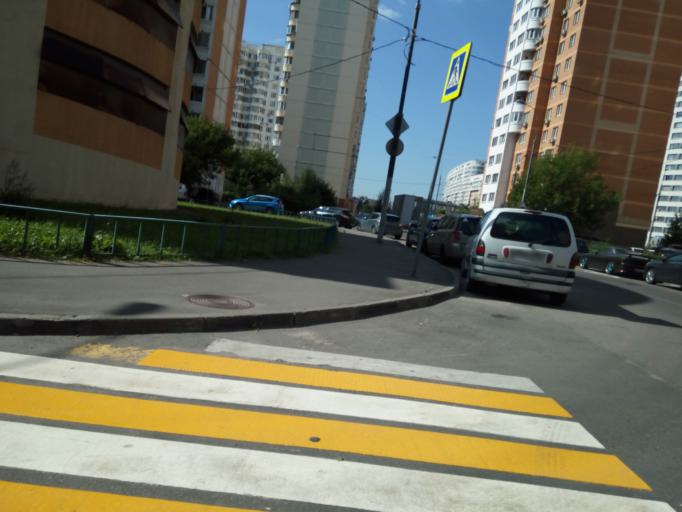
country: RU
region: Moscow
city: Sokol
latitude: 55.7812
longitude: 37.5328
